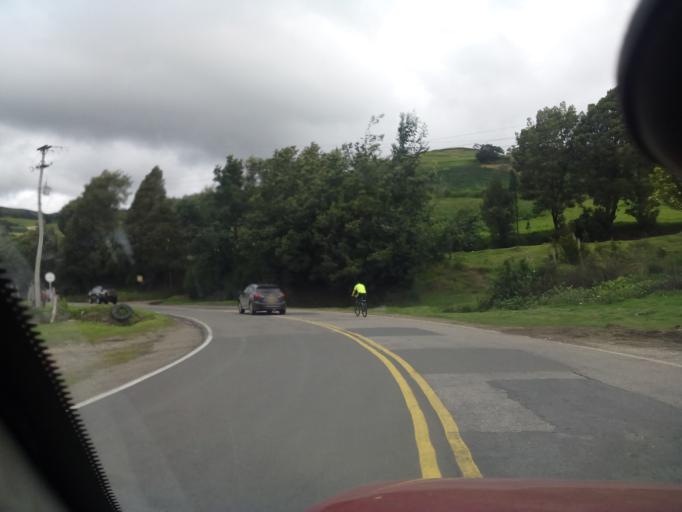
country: CO
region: Boyaca
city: Combita
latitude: 5.6647
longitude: -73.3597
